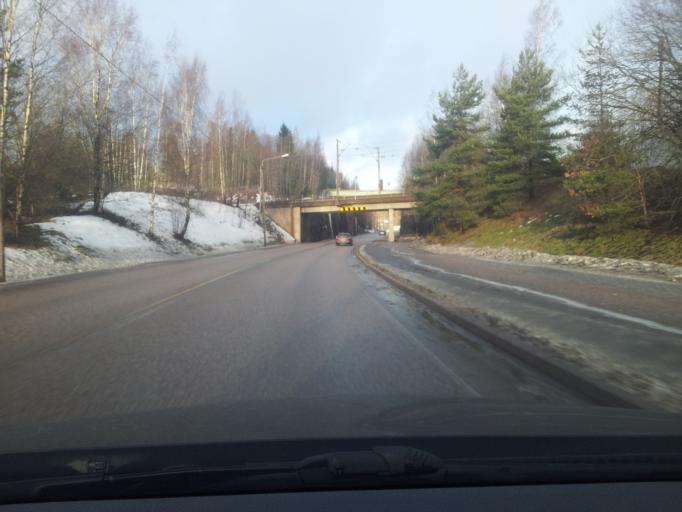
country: FI
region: Uusimaa
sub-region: Helsinki
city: Espoo
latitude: 60.1854
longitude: 24.5906
